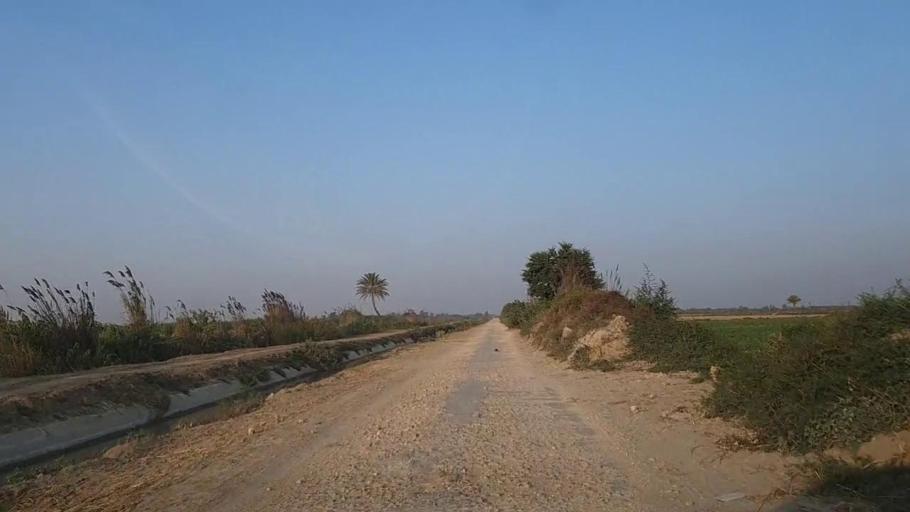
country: PK
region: Sindh
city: Keti Bandar
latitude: 24.2782
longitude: 67.6853
